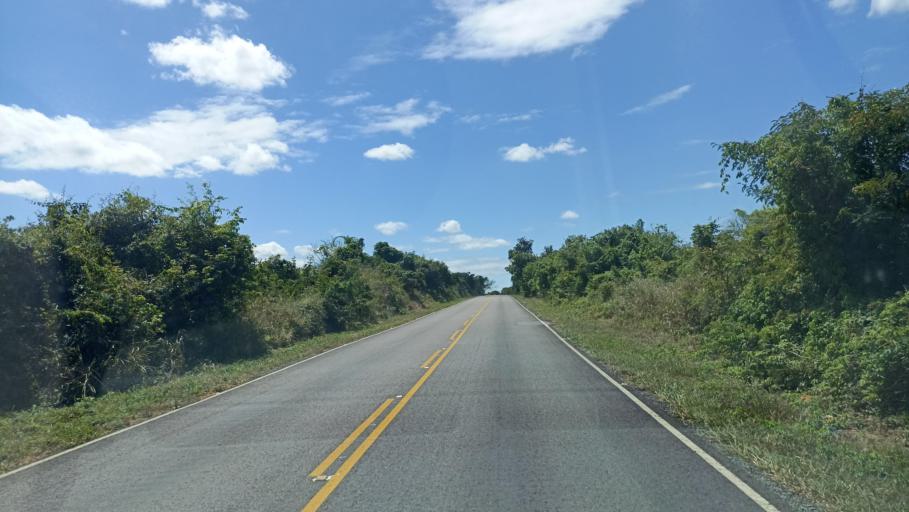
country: BR
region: Bahia
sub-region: Andarai
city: Vera Cruz
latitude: -12.7490
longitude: -41.3257
